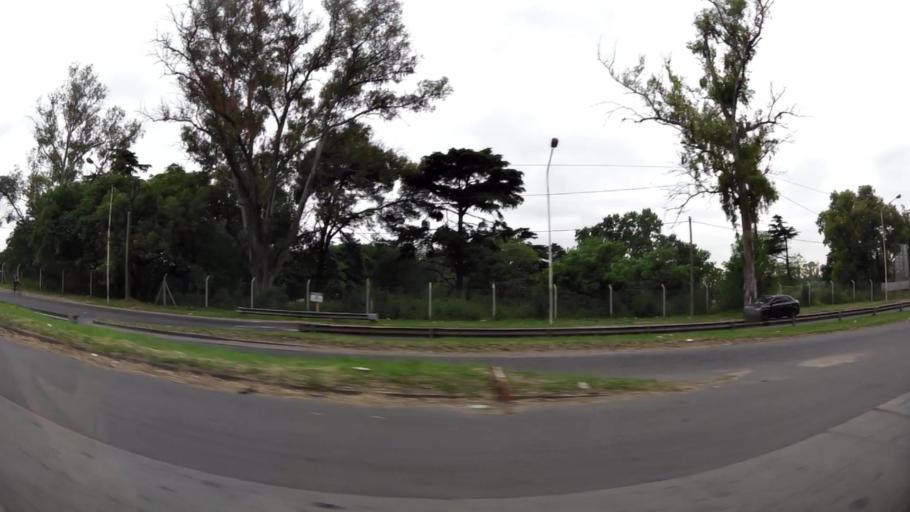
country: AR
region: Buenos Aires F.D.
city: Villa Lugano
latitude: -34.7192
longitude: -58.5162
